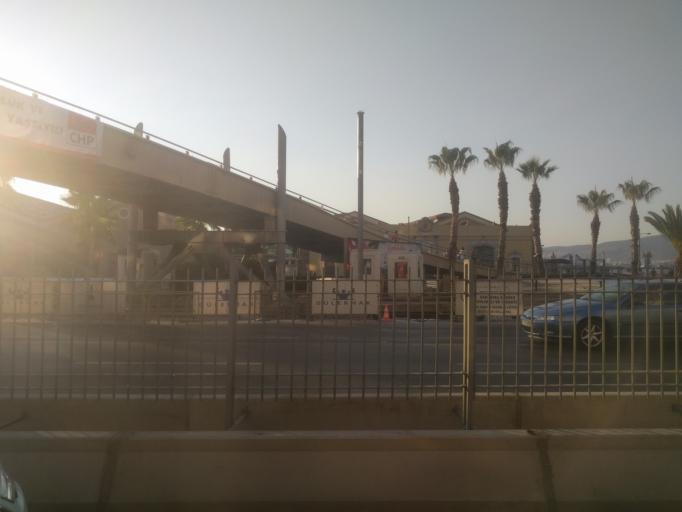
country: TR
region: Izmir
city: Izmir
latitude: 38.4220
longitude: 27.1306
